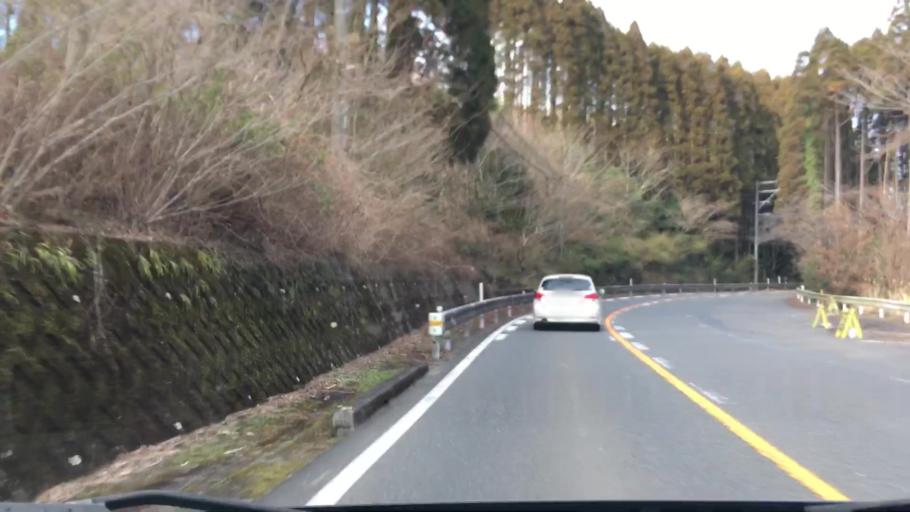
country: JP
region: Miyazaki
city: Nichinan
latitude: 31.7296
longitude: 131.3303
